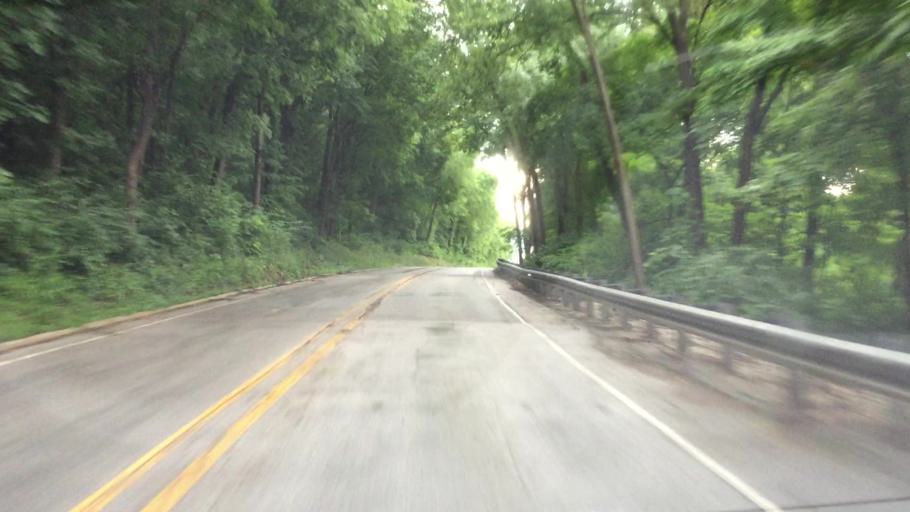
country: US
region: Illinois
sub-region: Hancock County
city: Hamilton
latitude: 40.4712
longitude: -91.3599
